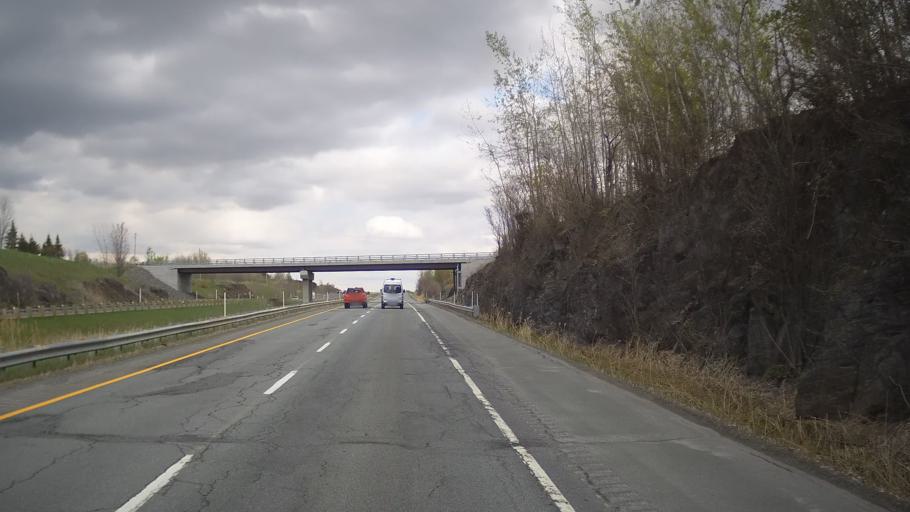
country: CA
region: Quebec
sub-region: Monteregie
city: Granby
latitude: 45.3407
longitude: -72.7483
